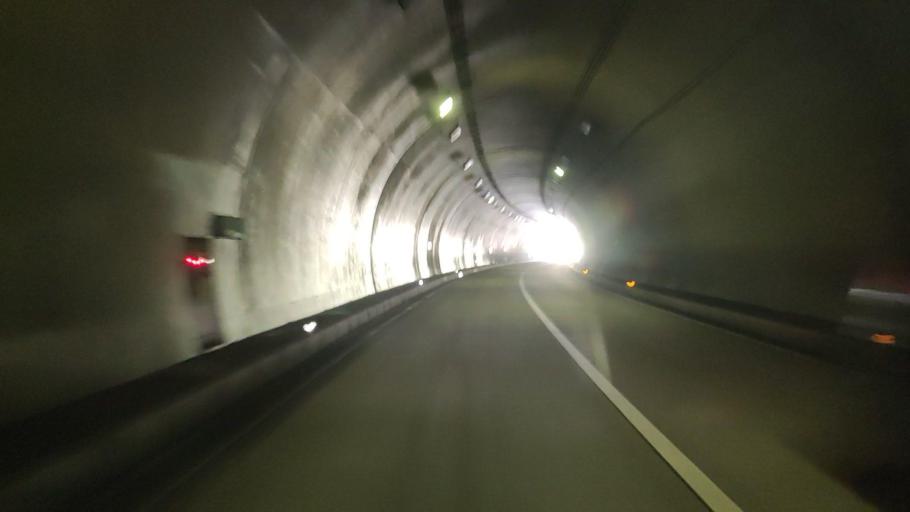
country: JP
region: Wakayama
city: Shingu
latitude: 33.8592
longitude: 135.8520
